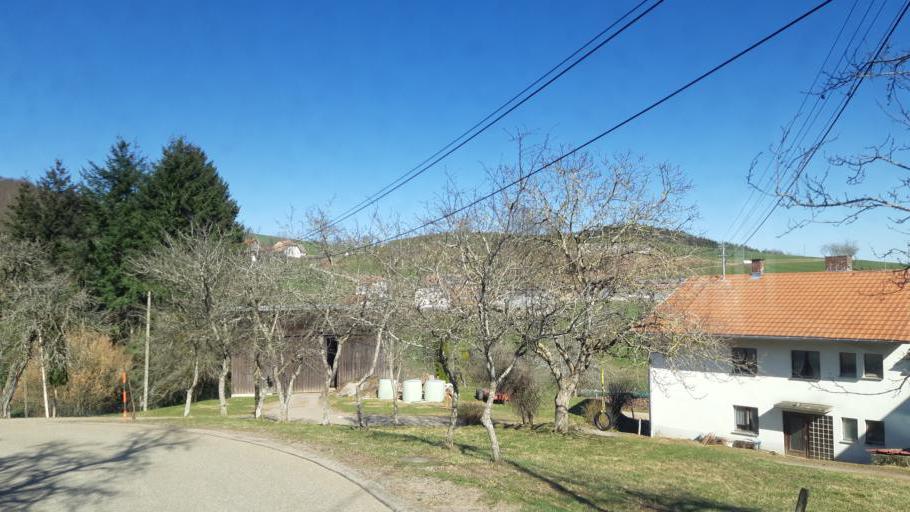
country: DE
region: Baden-Wuerttemberg
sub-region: Freiburg Region
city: Gutach im Breisgau
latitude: 48.1764
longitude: 7.9890
